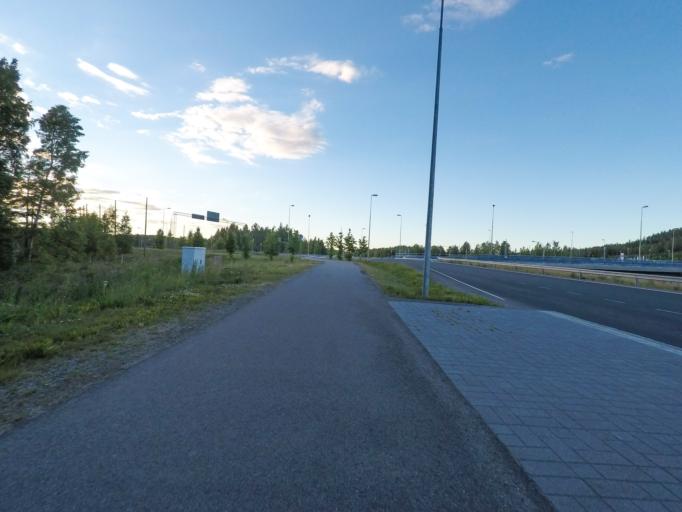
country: FI
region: Northern Savo
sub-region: Kuopio
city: Kuopio
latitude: 62.9721
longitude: 27.7045
